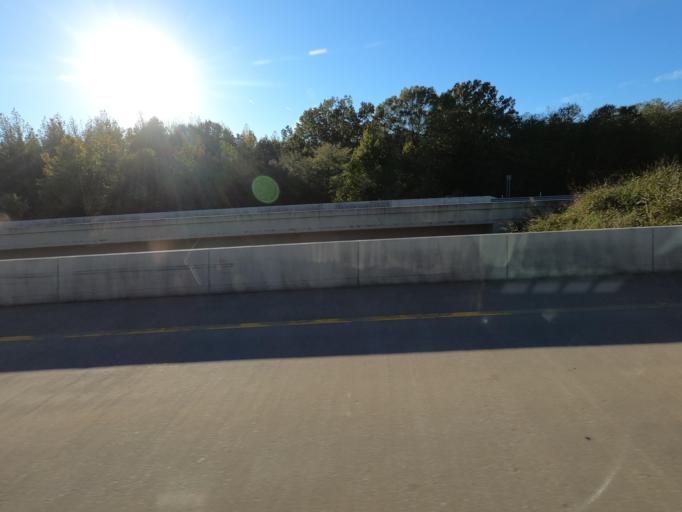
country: US
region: Tennessee
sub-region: Fayette County
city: Piperton
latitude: 35.1172
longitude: -89.6366
